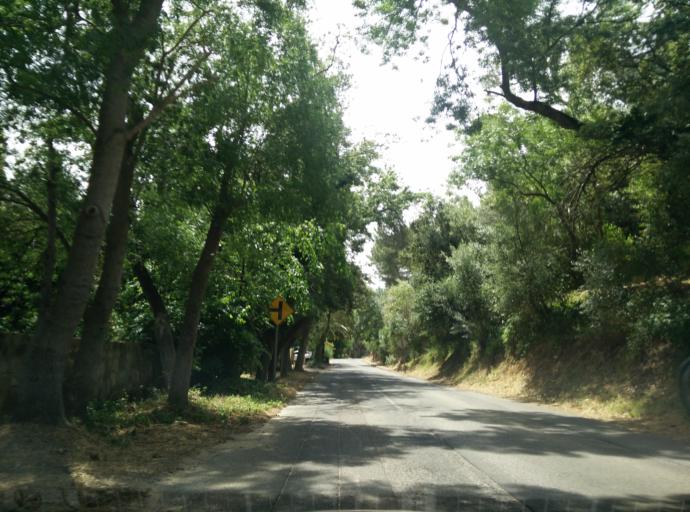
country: AU
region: South Australia
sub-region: Burnside
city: Beaumont
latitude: -34.9457
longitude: 138.6661
